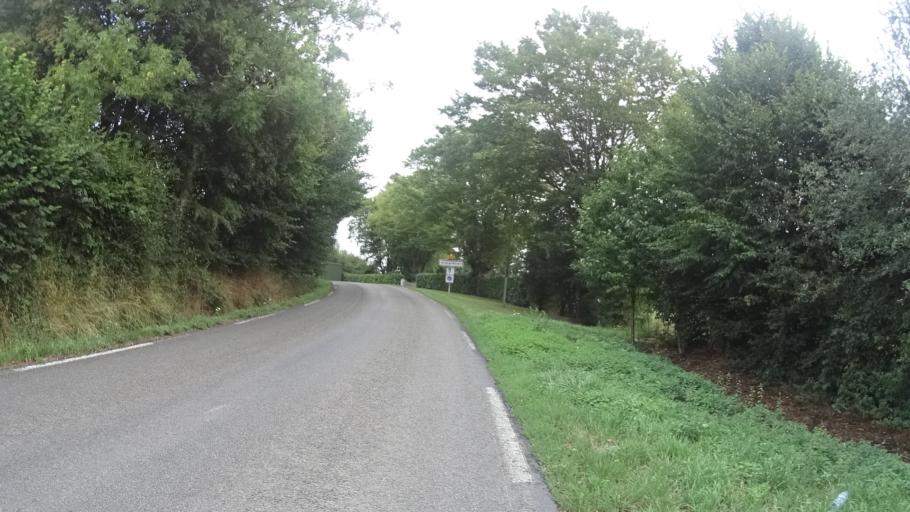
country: FR
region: Nord-Pas-de-Calais
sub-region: Departement du Nord
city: Berlaimont
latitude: 50.1905
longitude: 3.8077
